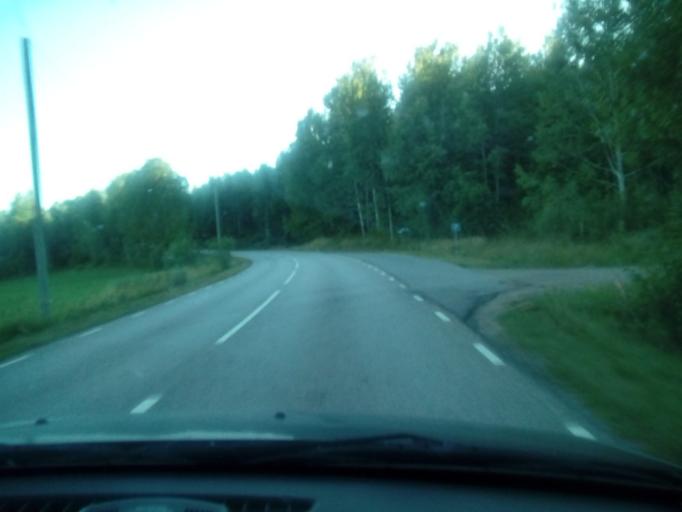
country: SE
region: Kalmar
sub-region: Vasterviks Kommun
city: Gamleby
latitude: 57.8123
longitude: 16.4362
